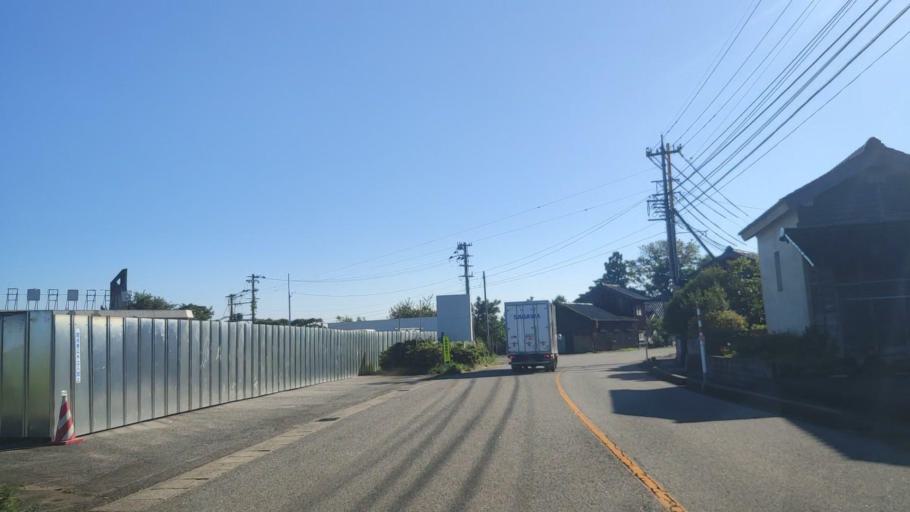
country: JP
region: Ishikawa
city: Nanao
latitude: 37.1933
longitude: 136.9106
